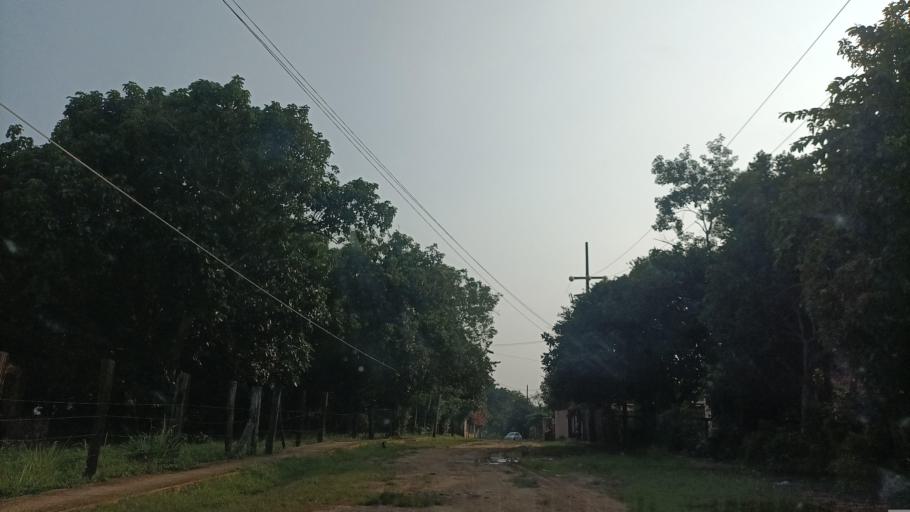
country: MX
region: Veracruz
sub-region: Cosoleacaque
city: Residencial las Olas
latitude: 18.1000
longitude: -94.5700
